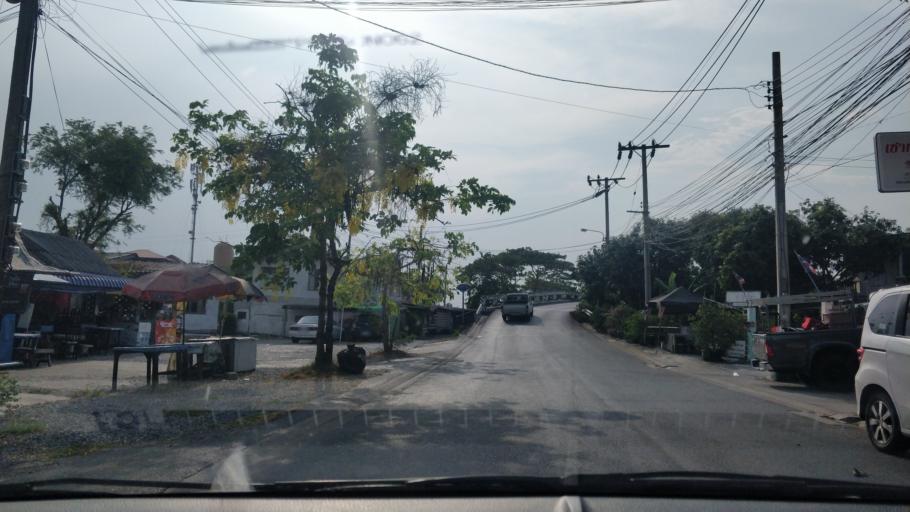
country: TH
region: Bangkok
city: Saphan Sung
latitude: 13.7345
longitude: 100.6966
